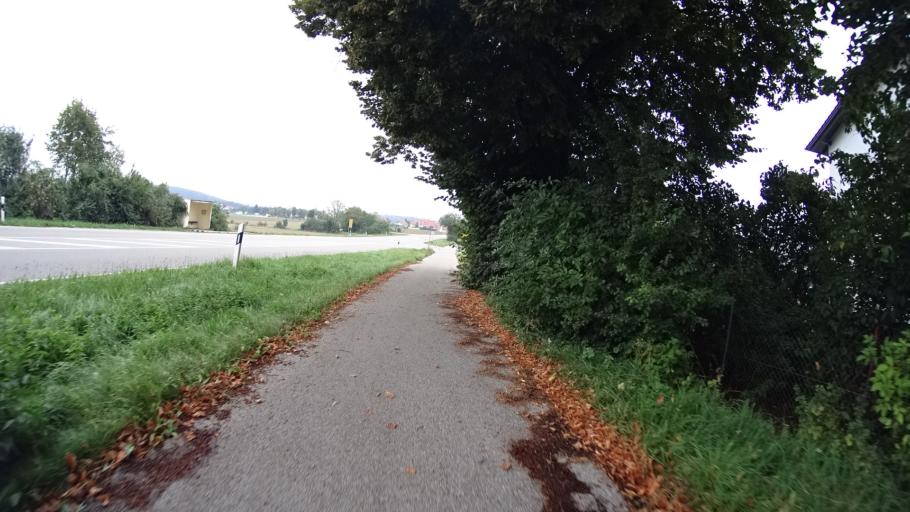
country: DE
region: Bavaria
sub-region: Upper Bavaria
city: Denkendorf
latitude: 48.9182
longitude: 11.4554
